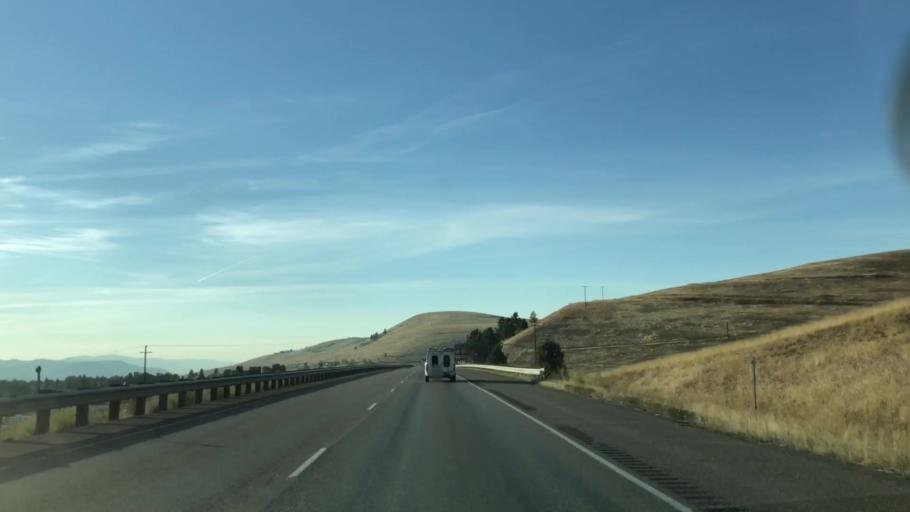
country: US
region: Montana
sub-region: Missoula County
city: Missoula
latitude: 46.9083
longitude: -114.0260
